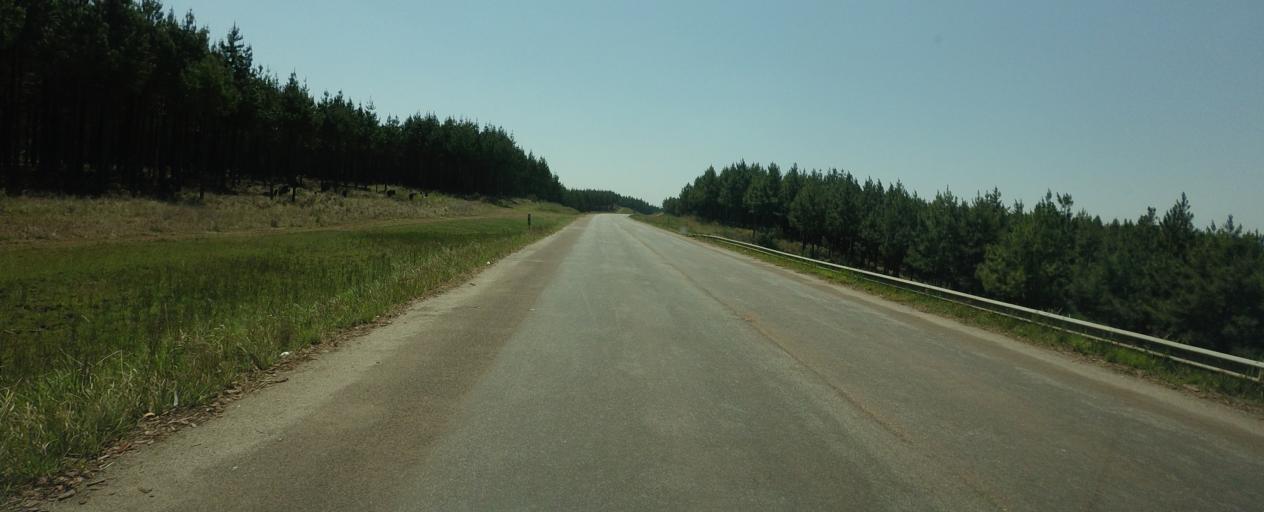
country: ZA
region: Mpumalanga
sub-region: Ehlanzeni District
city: Graksop
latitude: -24.9020
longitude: 30.8448
